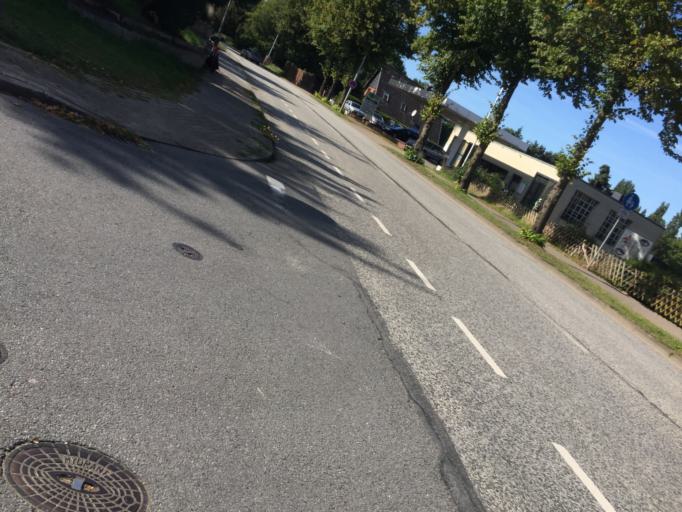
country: DE
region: Schleswig-Holstein
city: Itzehoe
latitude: 53.9112
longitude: 9.4929
